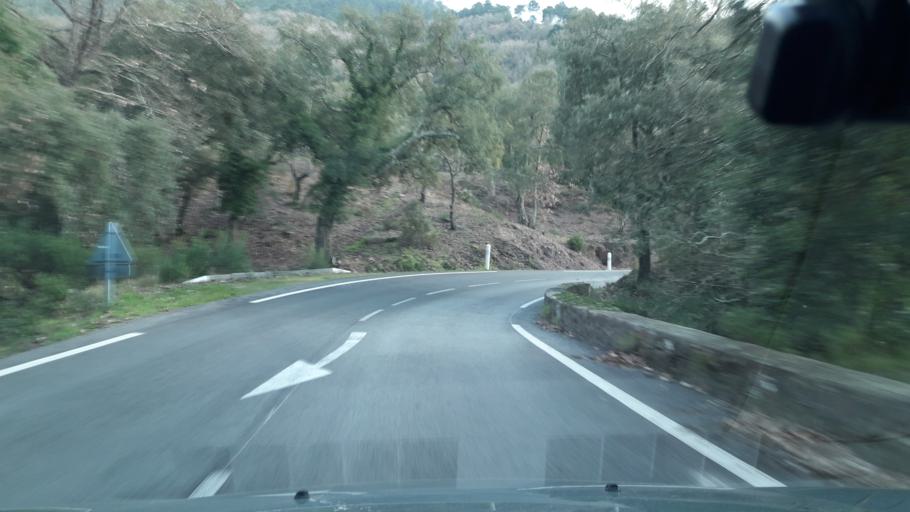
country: FR
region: Provence-Alpes-Cote d'Azur
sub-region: Departement du Var
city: Tanneron
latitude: 43.5167
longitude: 6.8371
